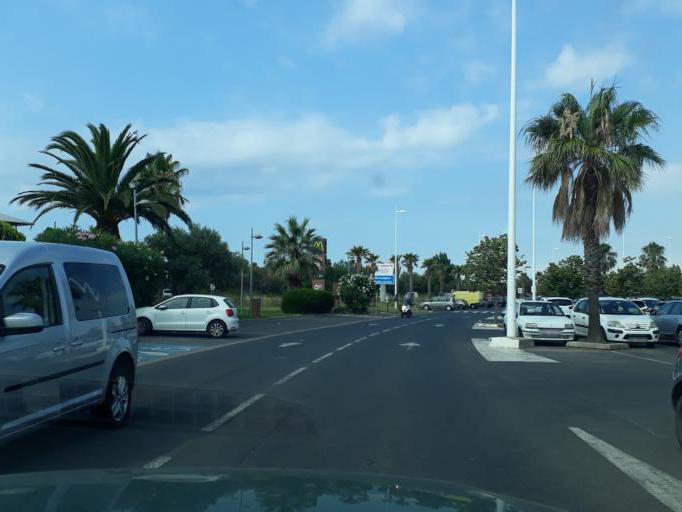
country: FR
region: Languedoc-Roussillon
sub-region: Departement de l'Herault
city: Agde
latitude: 43.2981
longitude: 3.4767
